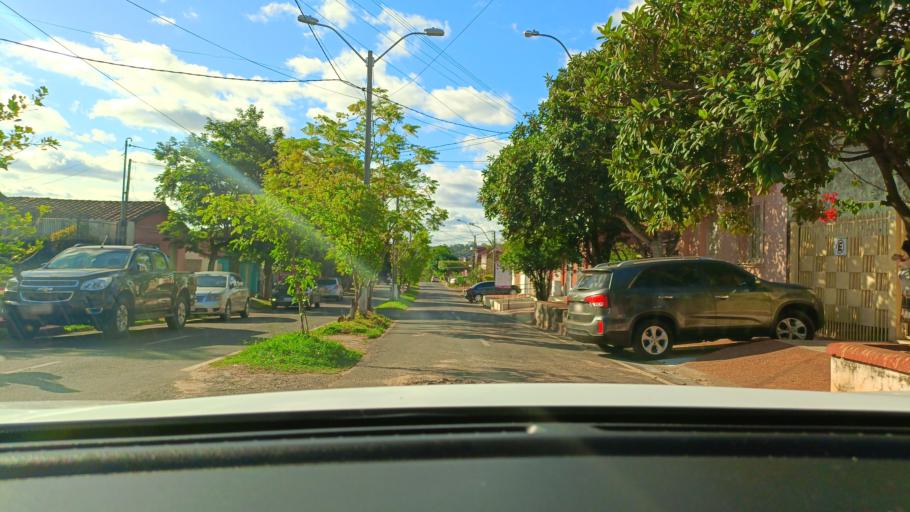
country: PY
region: San Pedro
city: Guayaybi
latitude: -24.6612
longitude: -56.4413
